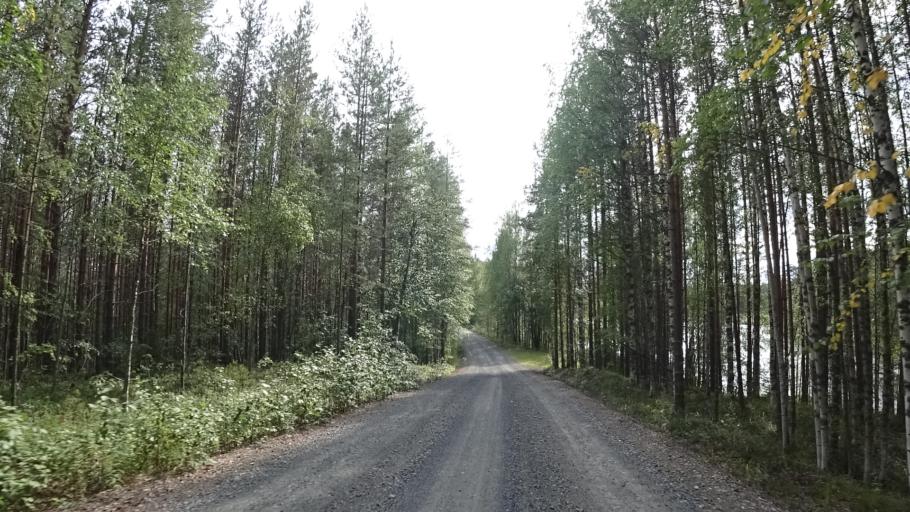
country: FI
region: North Karelia
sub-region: Joensuu
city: Ilomantsi
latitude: 62.6112
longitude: 31.1872
